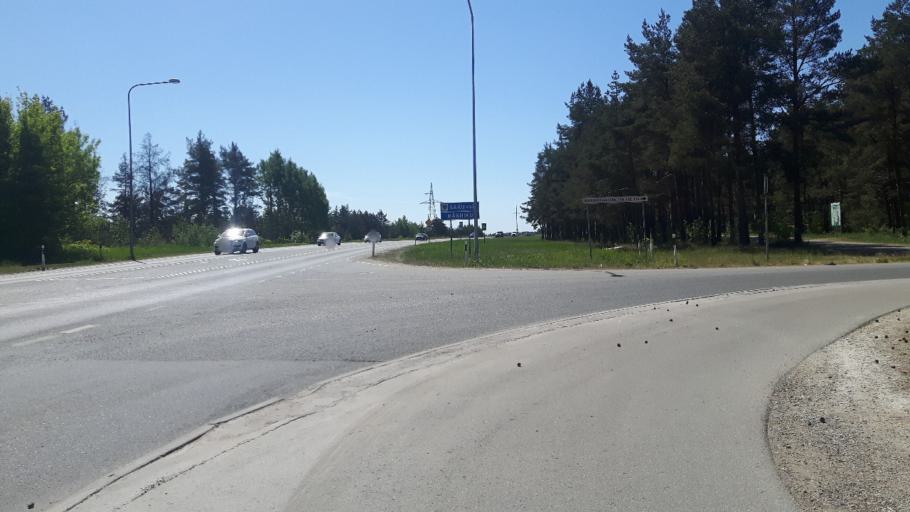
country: EE
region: Harju
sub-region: Tallinna linn
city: Tallinn
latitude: 59.3639
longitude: 24.7174
